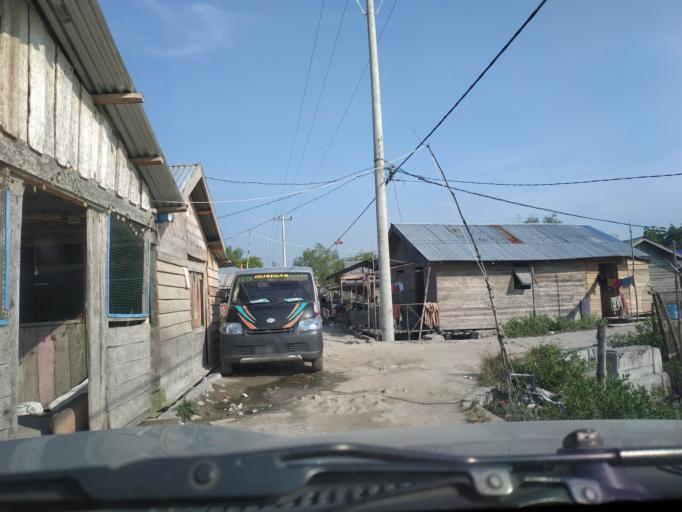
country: ID
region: North Sumatra
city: Teluk Nibung
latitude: 3.1096
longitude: 99.7784
